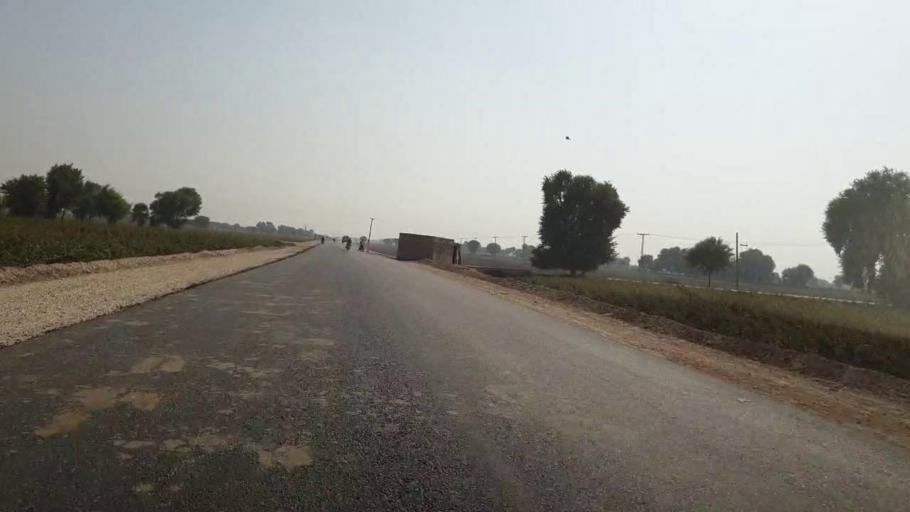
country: PK
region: Sindh
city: Dadu
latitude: 26.6690
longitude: 67.7765
